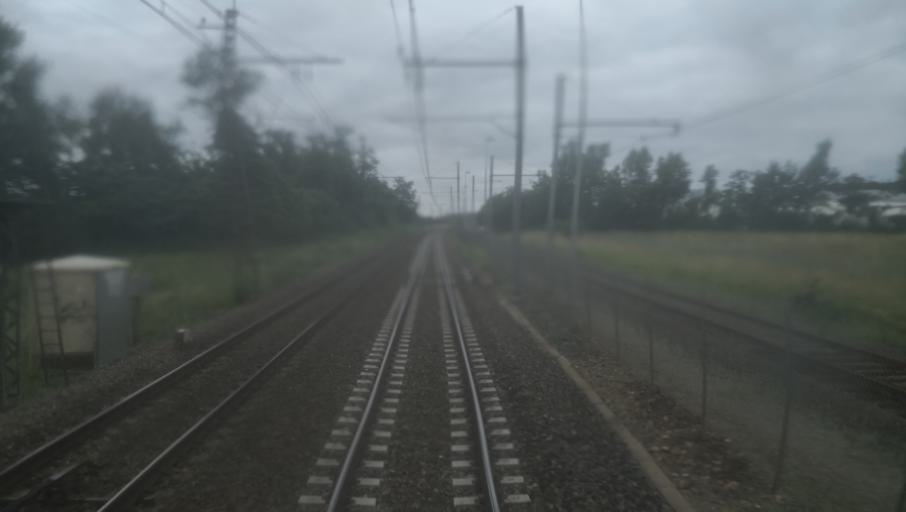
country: FR
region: Midi-Pyrenees
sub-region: Departement du Tarn-et-Garonne
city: Grisolles
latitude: 43.8428
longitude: 1.2918
